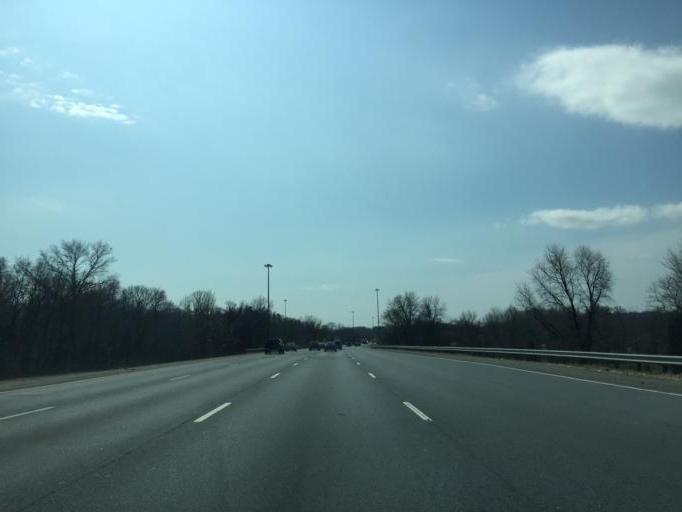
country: US
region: Maryland
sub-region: Baltimore County
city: Arbutus
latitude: 39.2512
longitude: -76.6809
